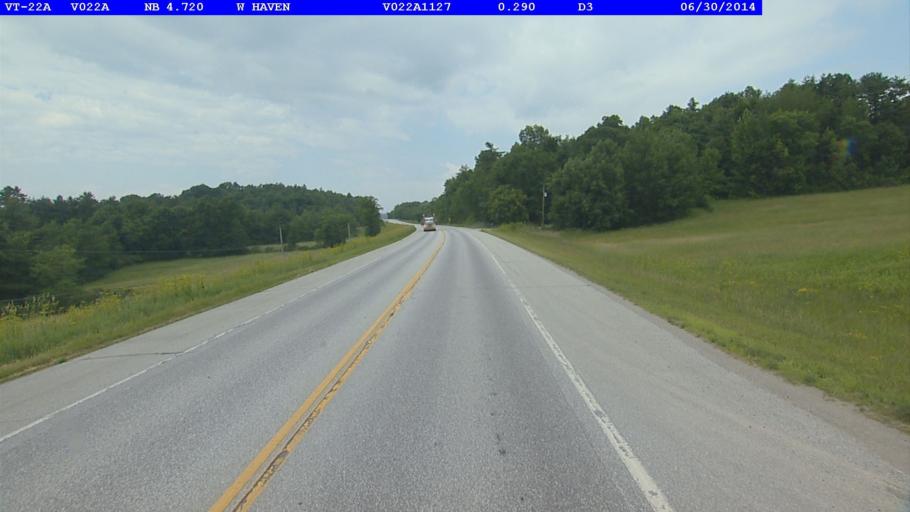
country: US
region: Vermont
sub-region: Rutland County
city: Fair Haven
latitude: 43.6325
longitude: -73.2967
